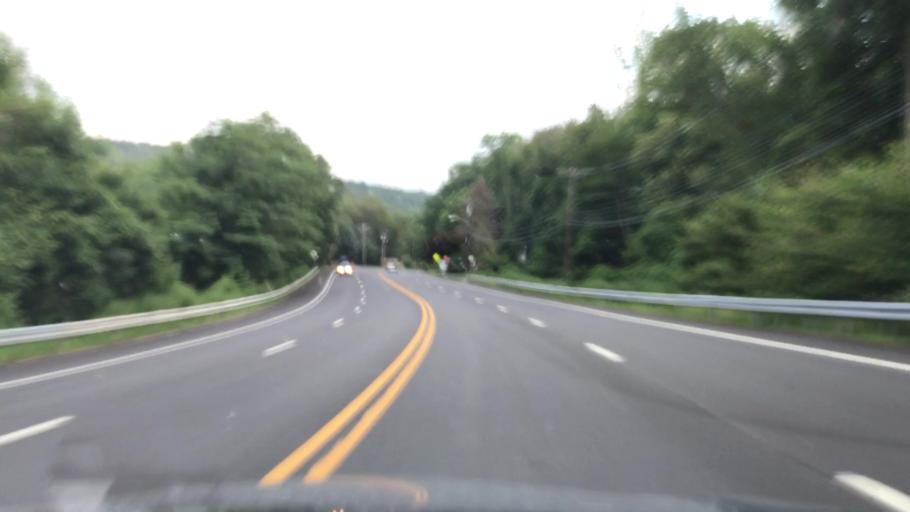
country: US
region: New York
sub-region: Rockland County
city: Sloatsburg
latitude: 41.2067
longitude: -74.1855
